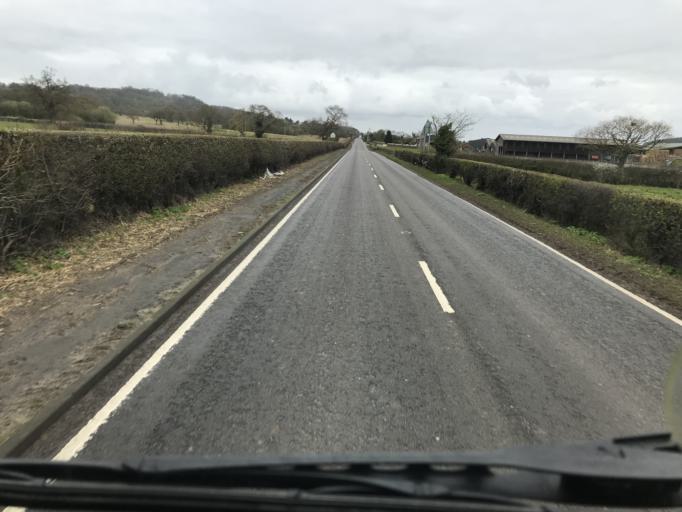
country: GB
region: England
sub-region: Cheshire West and Chester
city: Harthill
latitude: 53.0933
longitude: -2.7766
